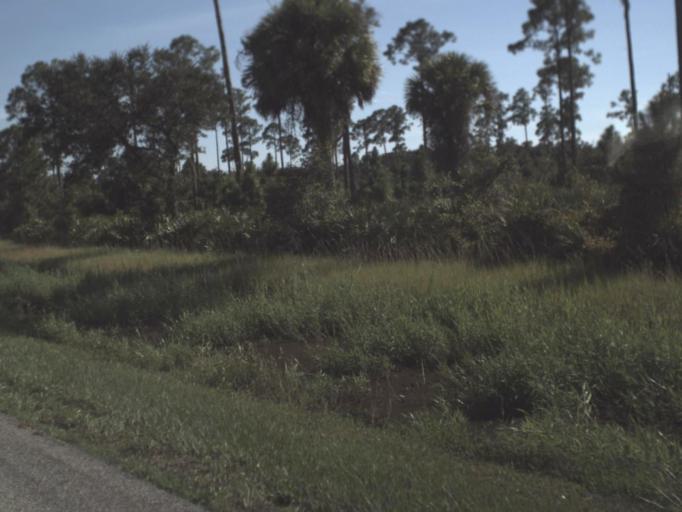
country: US
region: Florida
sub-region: Glades County
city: Moore Haven
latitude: 26.8996
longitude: -81.2397
